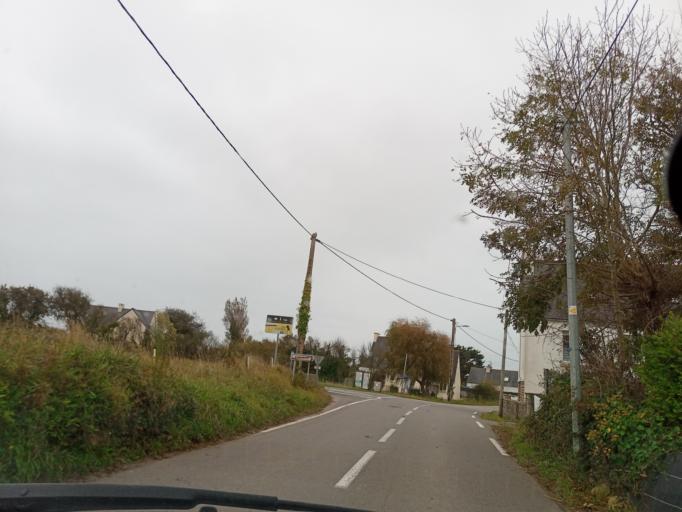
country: FR
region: Brittany
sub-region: Departement du Finistere
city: Esquibien
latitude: 48.0201
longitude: -4.5639
